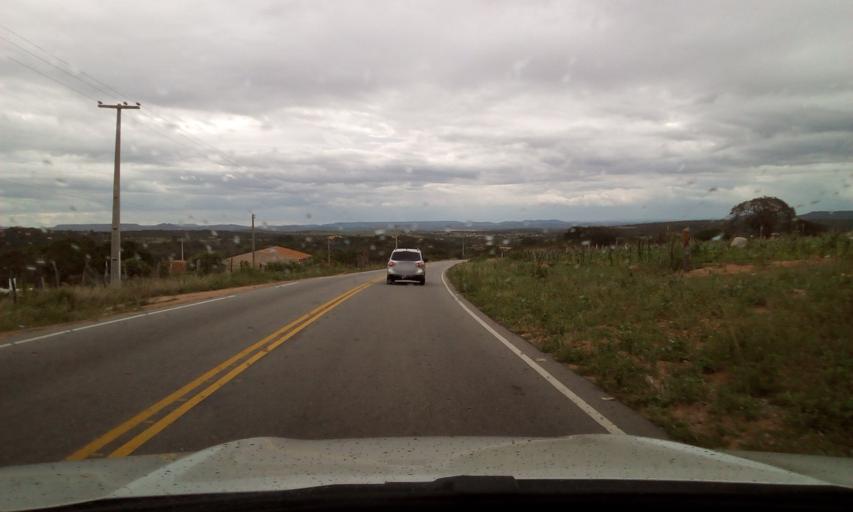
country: BR
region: Paraiba
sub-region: Picui
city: Picui
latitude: -6.5719
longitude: -36.2710
